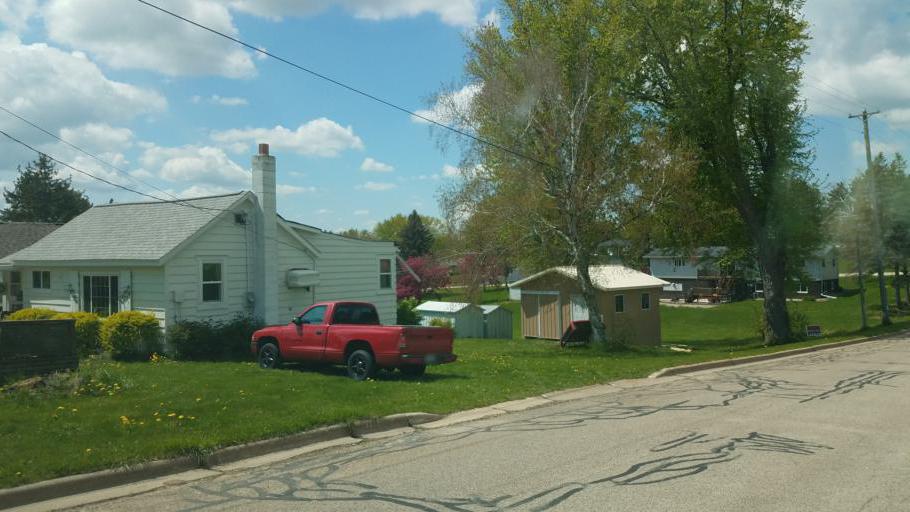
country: US
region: Wisconsin
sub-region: Vernon County
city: Hillsboro
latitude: 43.6584
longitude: -90.3456
